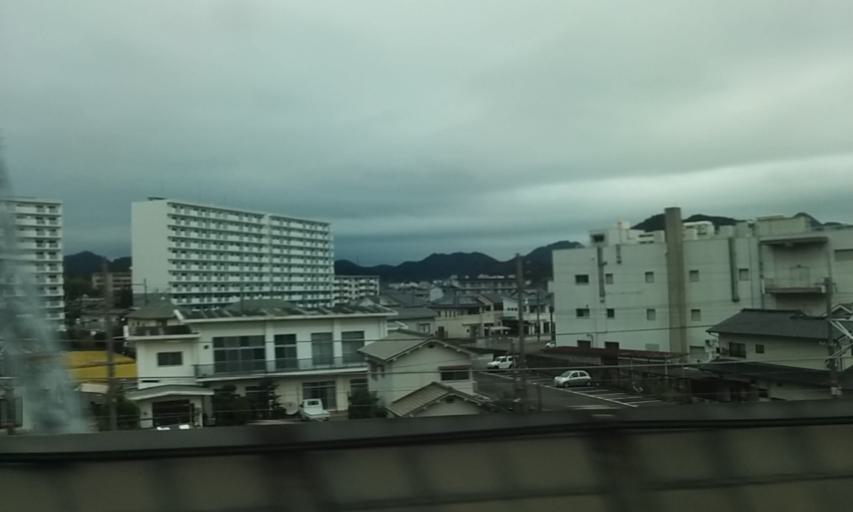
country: JP
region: Hyogo
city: Himeji
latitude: 34.8176
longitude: 134.7339
